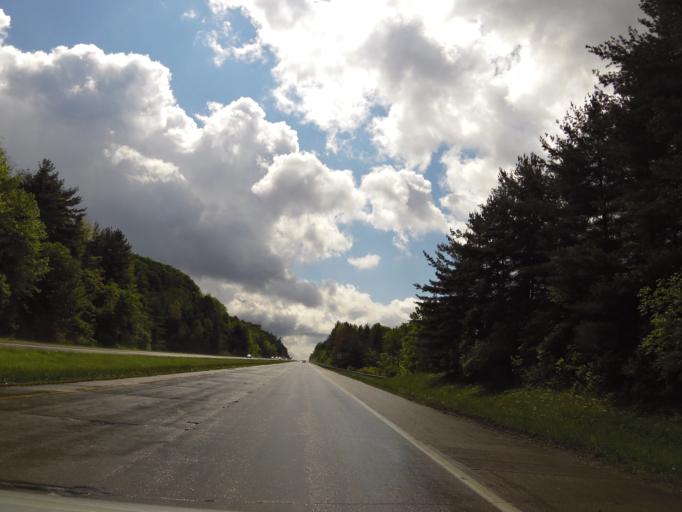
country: US
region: Ohio
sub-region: Athens County
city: Athens
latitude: 39.3582
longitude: -82.1014
